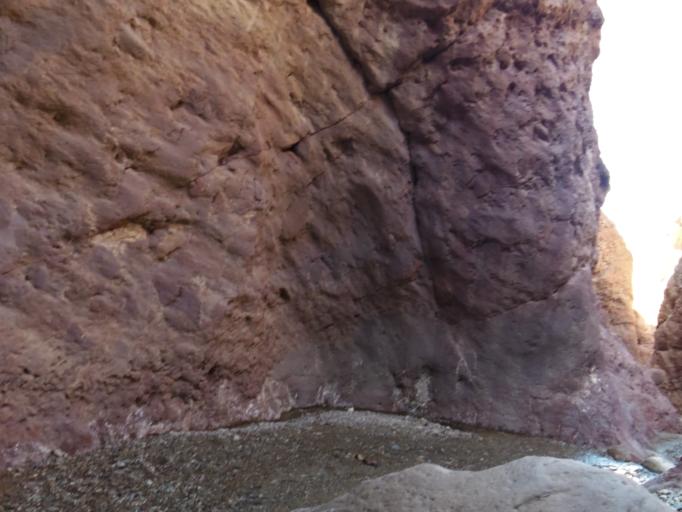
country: US
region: Nevada
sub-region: Clark County
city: Boulder City
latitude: 35.9602
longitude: -114.7263
